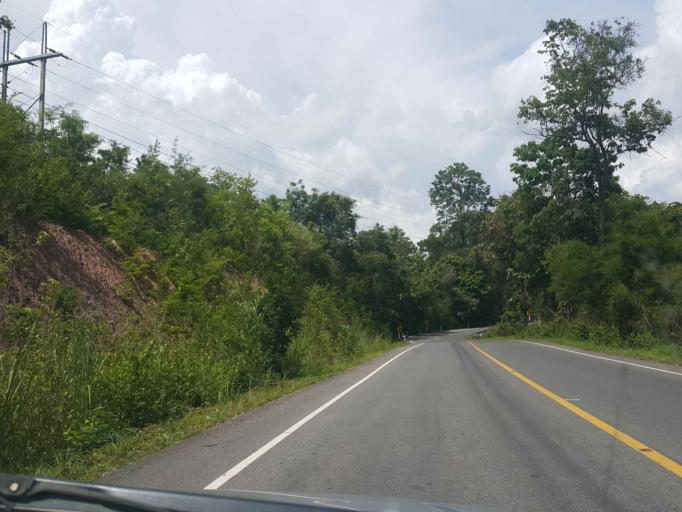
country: TH
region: Nan
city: Ban Luang
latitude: 18.8737
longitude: 100.5234
